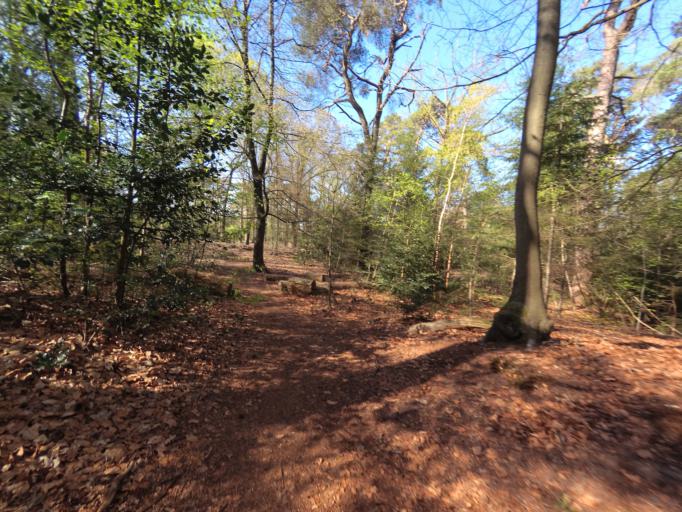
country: NL
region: Utrecht
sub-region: Gemeente Amersfoort
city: Amersfoort
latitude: 52.1342
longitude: 5.3815
